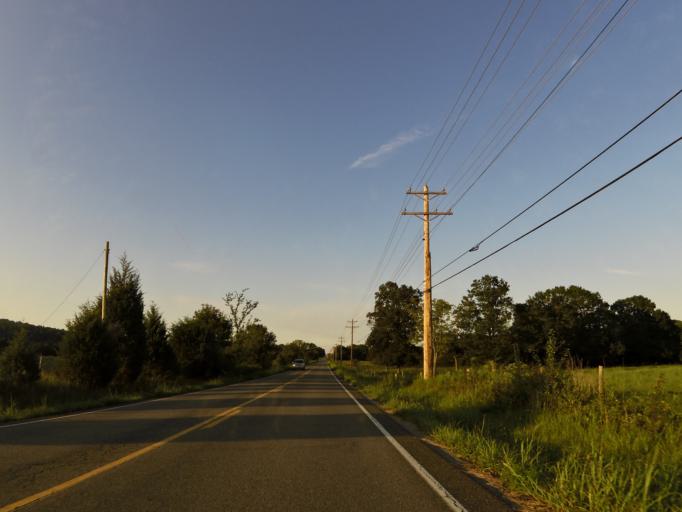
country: US
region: Tennessee
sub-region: Roane County
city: Rockwood
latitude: 35.6912
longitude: -84.6607
